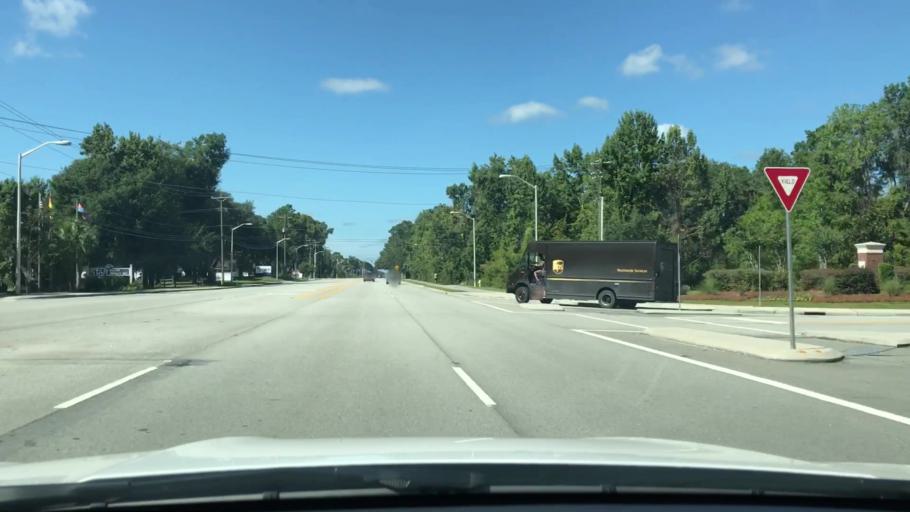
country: US
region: South Carolina
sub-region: Charleston County
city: Shell Point
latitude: 32.8335
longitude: -80.0686
